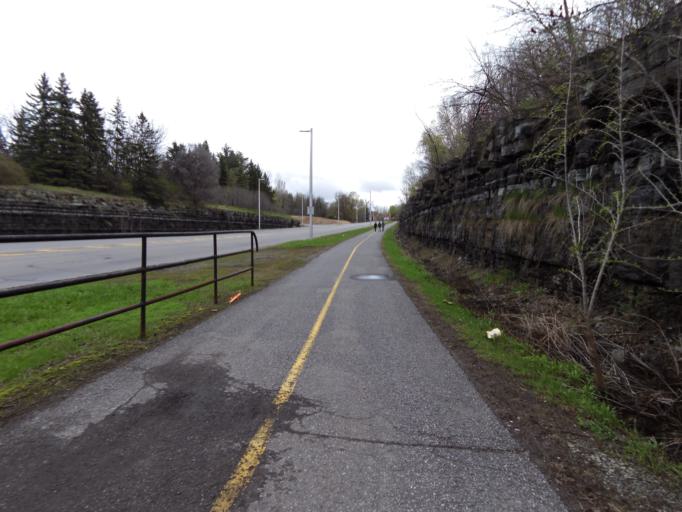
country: CA
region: Ontario
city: Bells Corners
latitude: 45.3587
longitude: -75.7717
